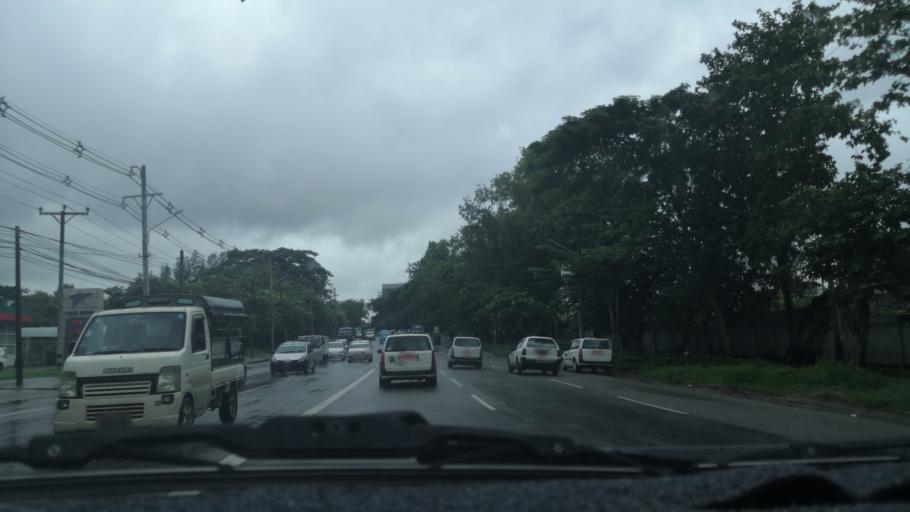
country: MM
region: Yangon
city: Yangon
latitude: 16.8968
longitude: 96.1225
